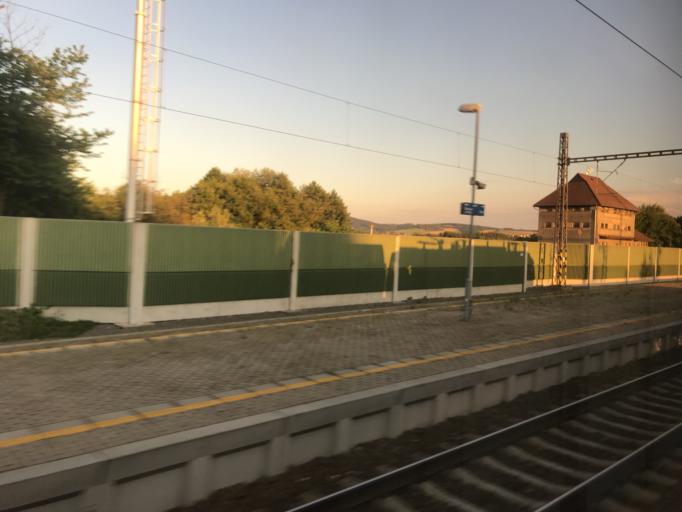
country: CZ
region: Central Bohemia
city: Votice
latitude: 49.6690
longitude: 14.6252
